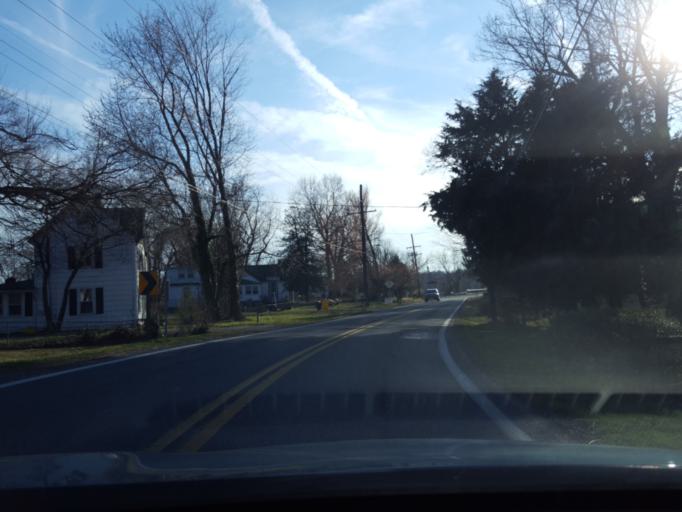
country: US
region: Maryland
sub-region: Anne Arundel County
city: Deale
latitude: 38.7794
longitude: -76.5606
